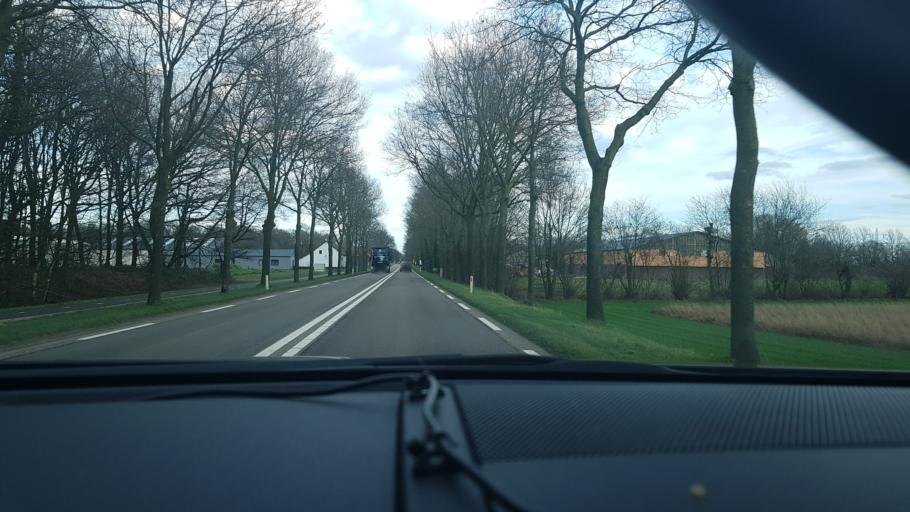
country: NL
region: Limburg
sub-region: Gemeente Beesel
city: Beesel
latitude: 51.2725
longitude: 6.0033
